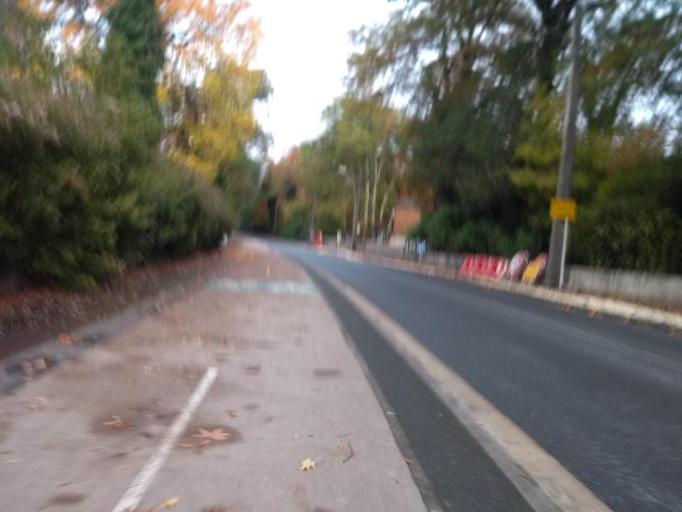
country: FR
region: Aquitaine
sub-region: Departement de la Gironde
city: Canejan
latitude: 44.7647
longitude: -0.6415
